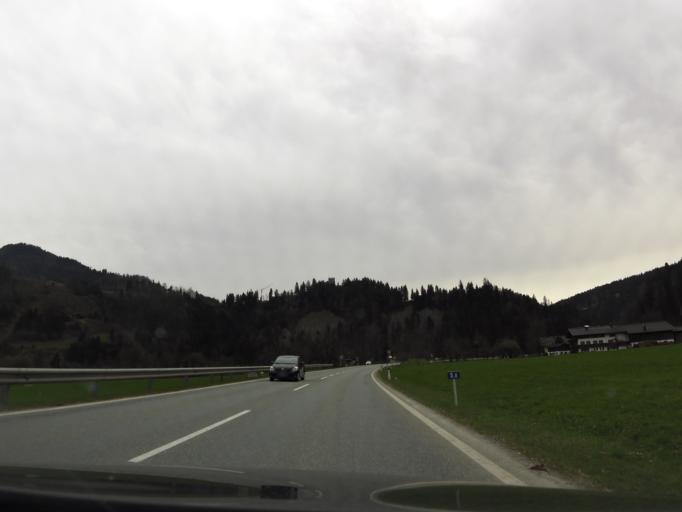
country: AT
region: Tyrol
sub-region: Politischer Bezirk Kitzbuhel
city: Itter
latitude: 47.4770
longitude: 12.1340
